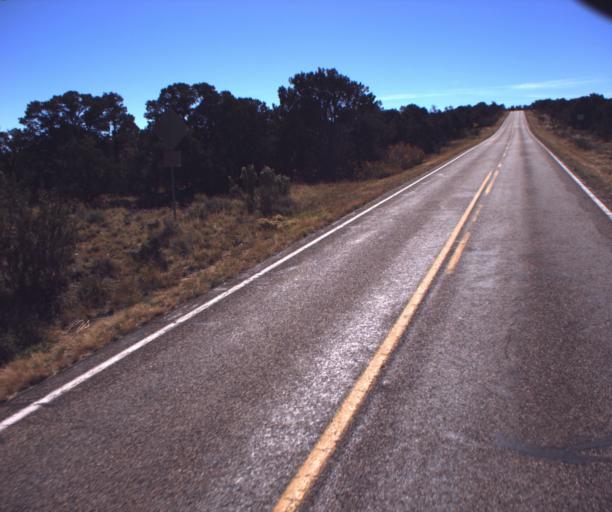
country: US
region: Arizona
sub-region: Coconino County
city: Fredonia
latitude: 36.8215
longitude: -112.2536
